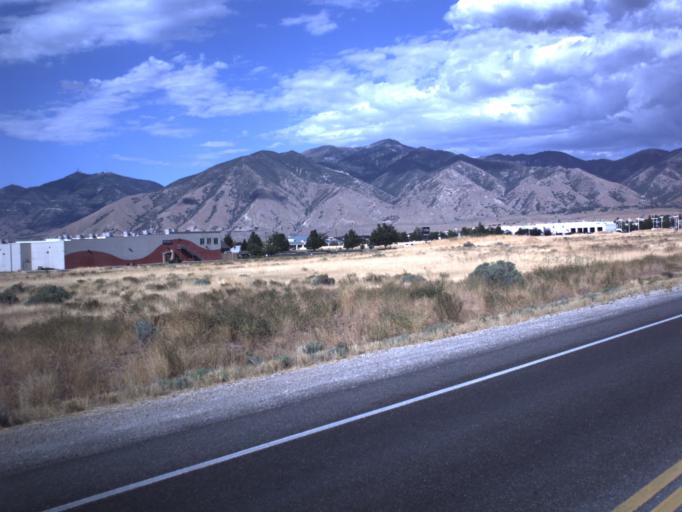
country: US
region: Utah
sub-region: Tooele County
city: Tooele
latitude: 40.5510
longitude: -112.3051
